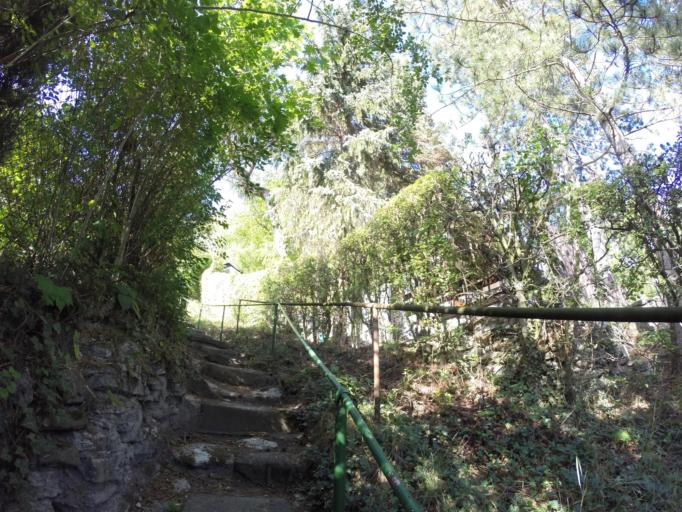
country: DE
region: Thuringia
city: Jena
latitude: 50.9348
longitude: 11.6157
